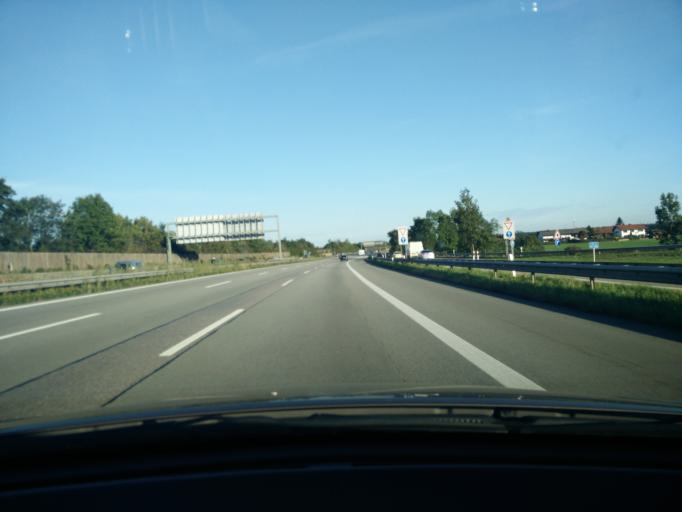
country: DE
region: Bavaria
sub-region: Upper Bavaria
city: Holzkirchen
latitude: 47.8957
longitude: 11.7247
